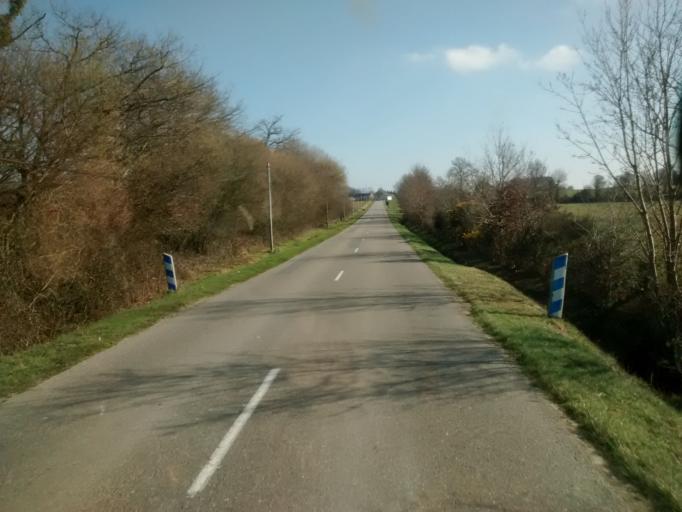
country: FR
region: Brittany
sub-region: Departement d'Ille-et-Vilaine
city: Maxent
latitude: 47.9718
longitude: -2.0203
